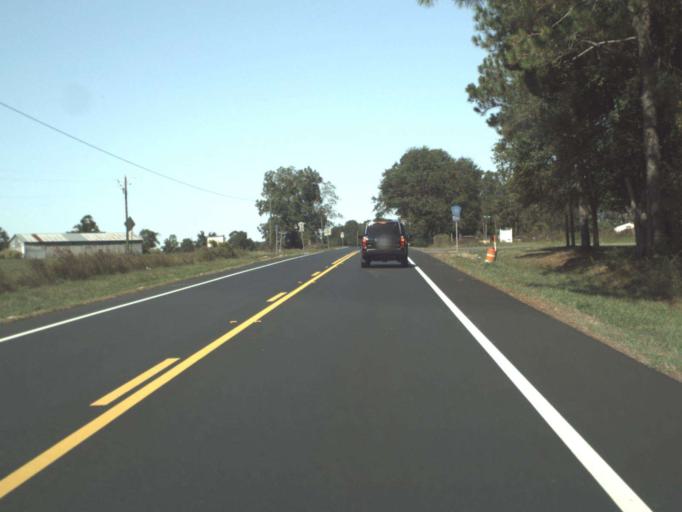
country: US
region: Florida
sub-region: Walton County
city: DeFuniak Springs
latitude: 30.8087
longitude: -86.1999
